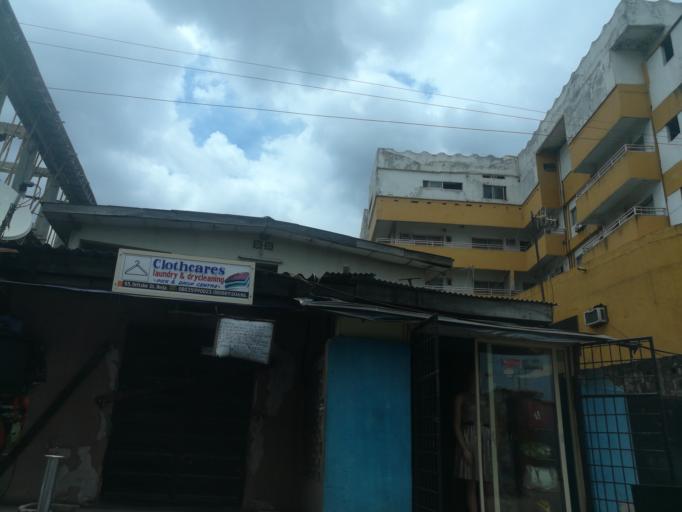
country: NG
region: Lagos
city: Ikeja
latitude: 6.6045
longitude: 3.3473
